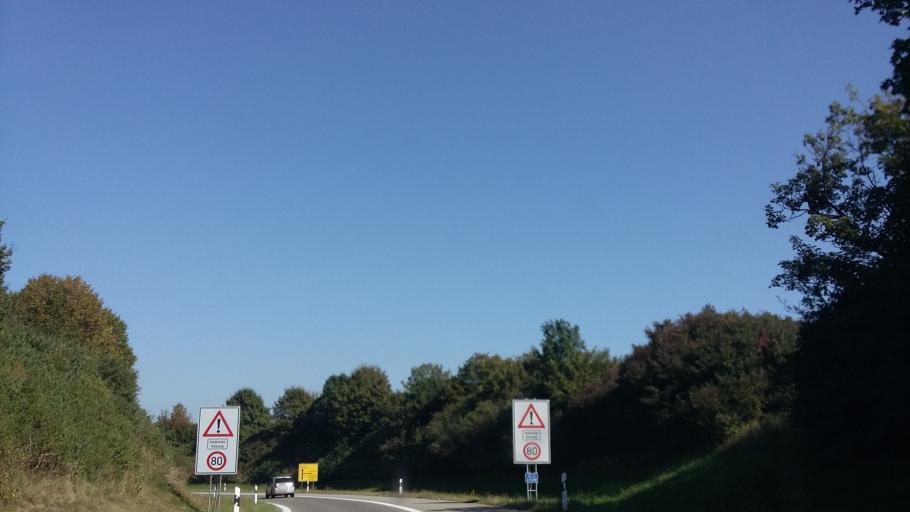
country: DE
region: Bavaria
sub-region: Upper Bavaria
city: Gilching
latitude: 48.0952
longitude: 11.3059
